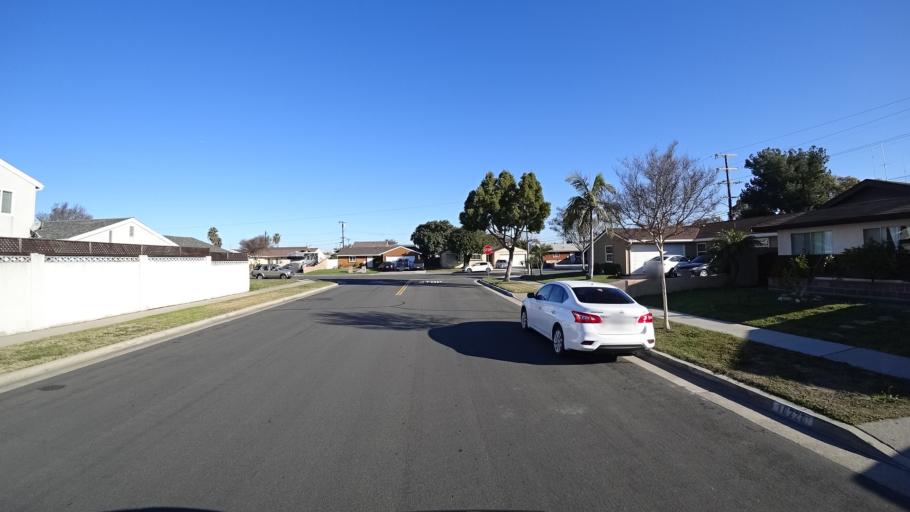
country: US
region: California
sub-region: Orange County
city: Cypress
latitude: 33.8139
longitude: -118.0177
